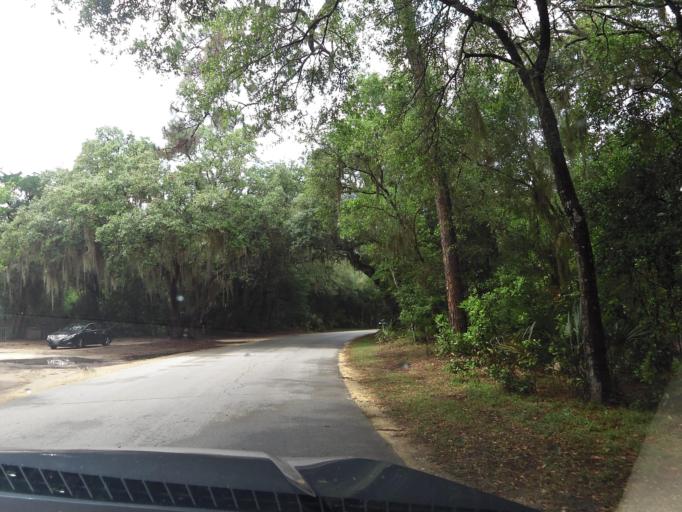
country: US
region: Florida
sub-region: Nassau County
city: Fernandina Beach
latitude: 30.6982
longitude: -81.4433
